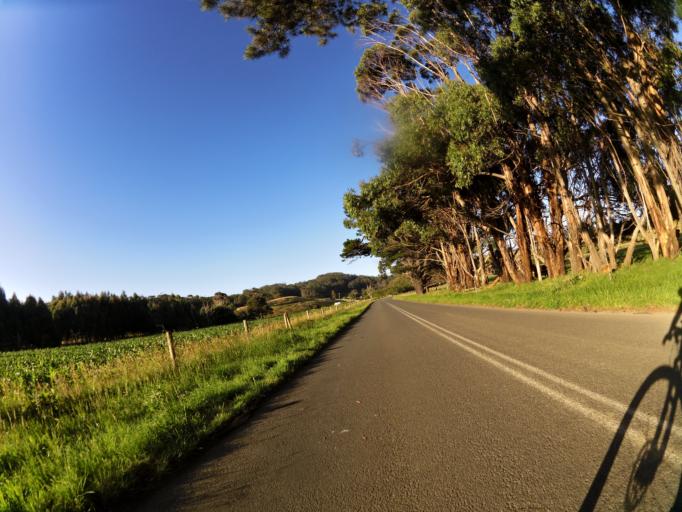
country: AU
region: Victoria
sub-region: Colac-Otway
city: Apollo Bay
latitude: -38.7685
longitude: 143.6513
